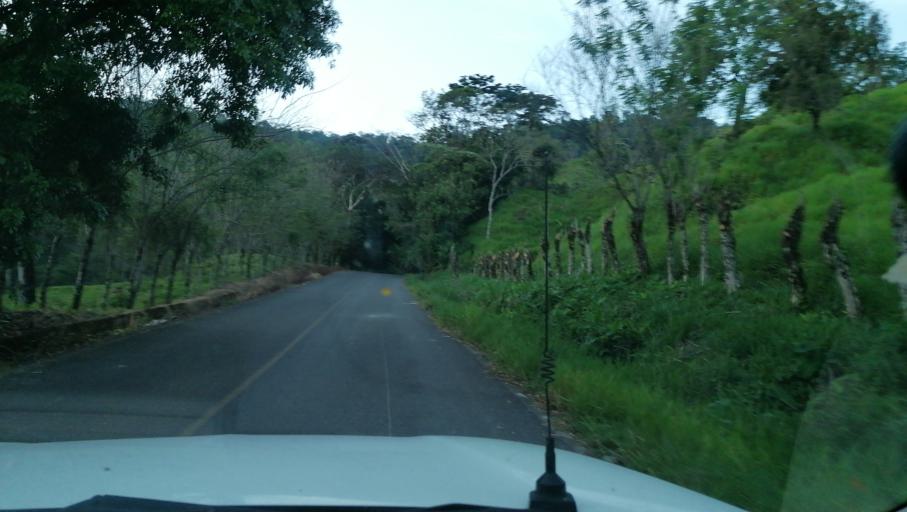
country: MX
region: Chiapas
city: Ostuacan
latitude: 17.4232
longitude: -93.3371
